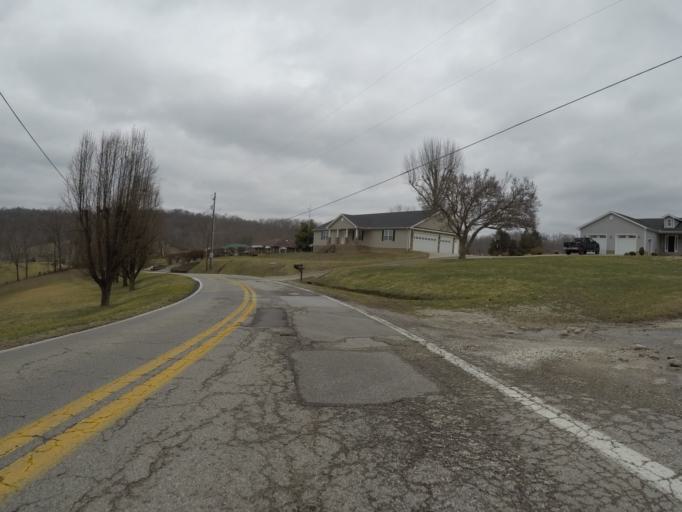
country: US
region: West Virginia
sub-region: Cabell County
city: Barboursville
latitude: 38.4324
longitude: -82.2429
